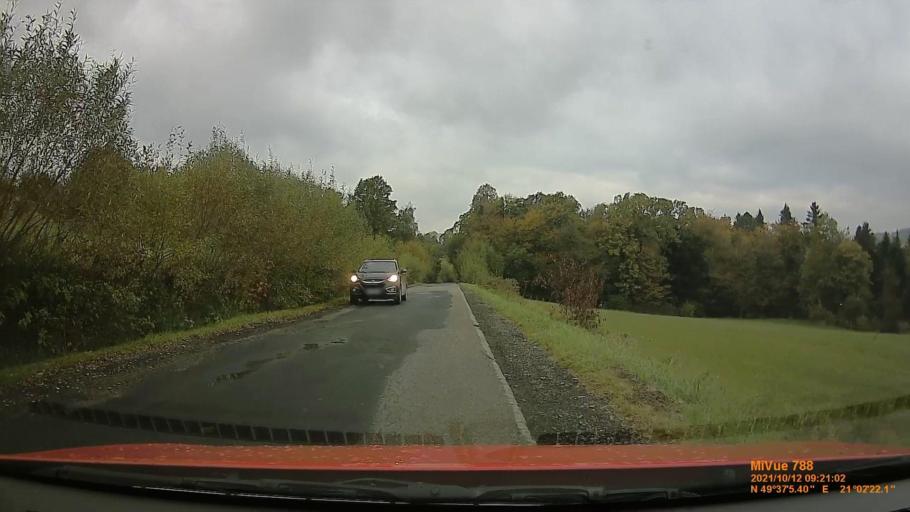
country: PL
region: Lesser Poland Voivodeship
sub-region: Powiat gorlicki
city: Ropa
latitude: 49.6182
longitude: 21.0393
